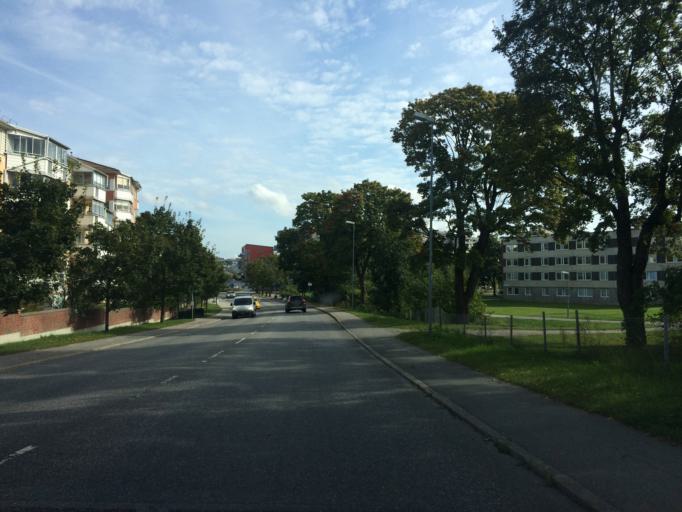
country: SE
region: Stockholm
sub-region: Sollentuna Kommun
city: Sollentuna
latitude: 59.4301
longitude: 17.9395
